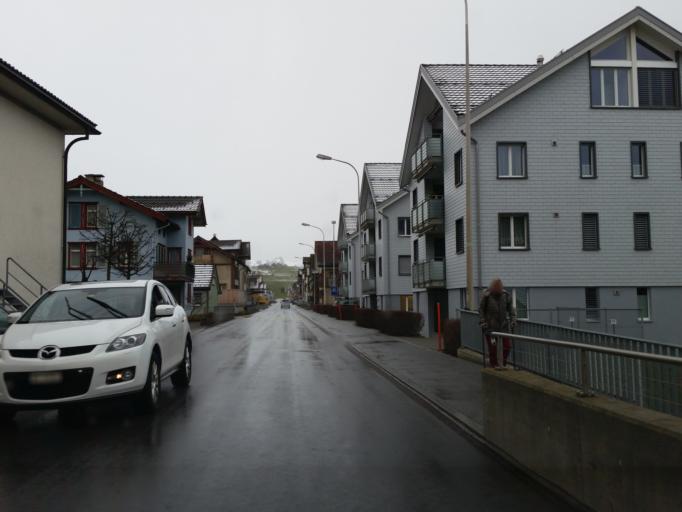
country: CH
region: Appenzell Innerrhoden
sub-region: Appenzell Inner Rhodes
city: Appenzell
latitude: 47.3319
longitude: 9.4039
